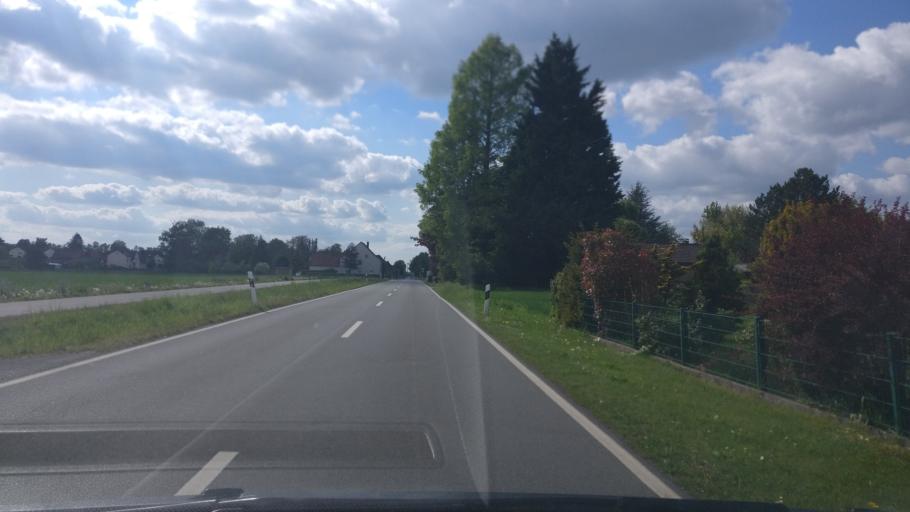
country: DE
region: North Rhine-Westphalia
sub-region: Regierungsbezirk Detmold
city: Leopoldshohe
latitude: 52.0066
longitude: 8.7128
